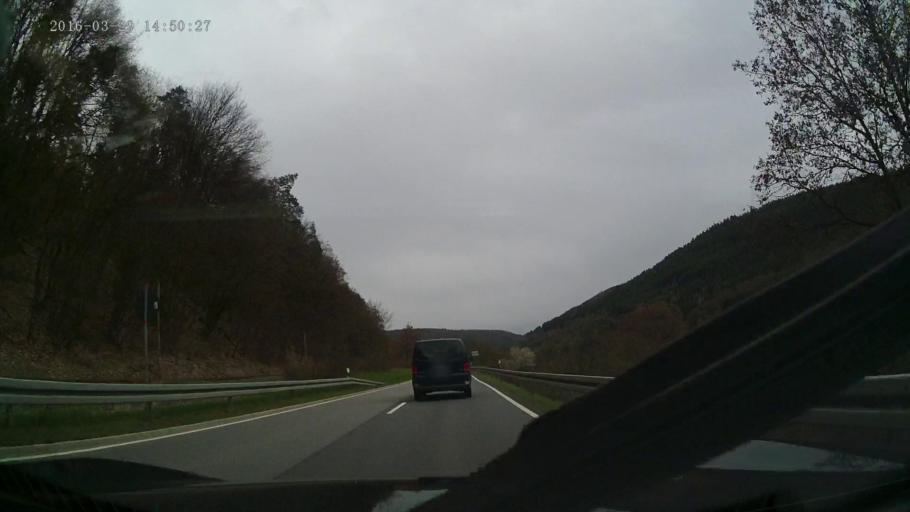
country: DE
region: Bavaria
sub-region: Regierungsbezirk Unterfranken
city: Weilbach
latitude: 49.6353
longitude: 9.2722
